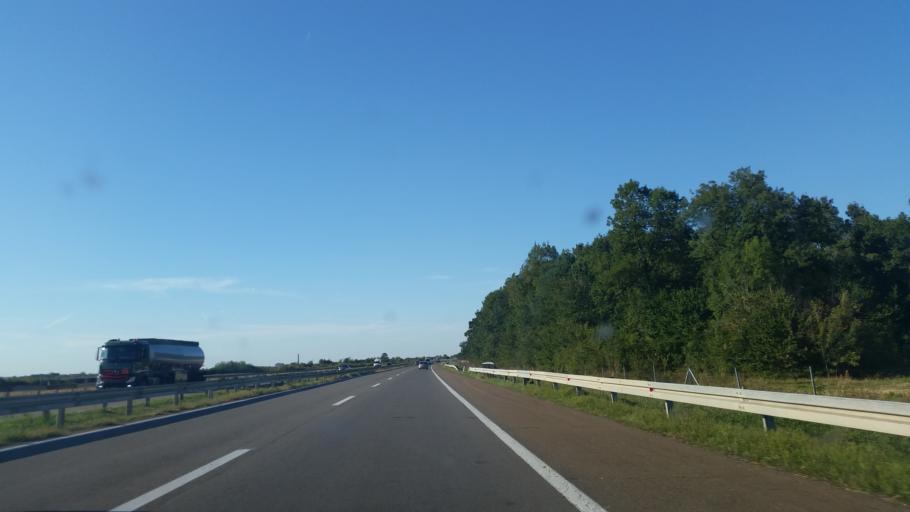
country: RS
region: Central Serbia
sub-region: Pomoravski Okrug
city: Paracin
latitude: 43.8894
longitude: 21.3983
